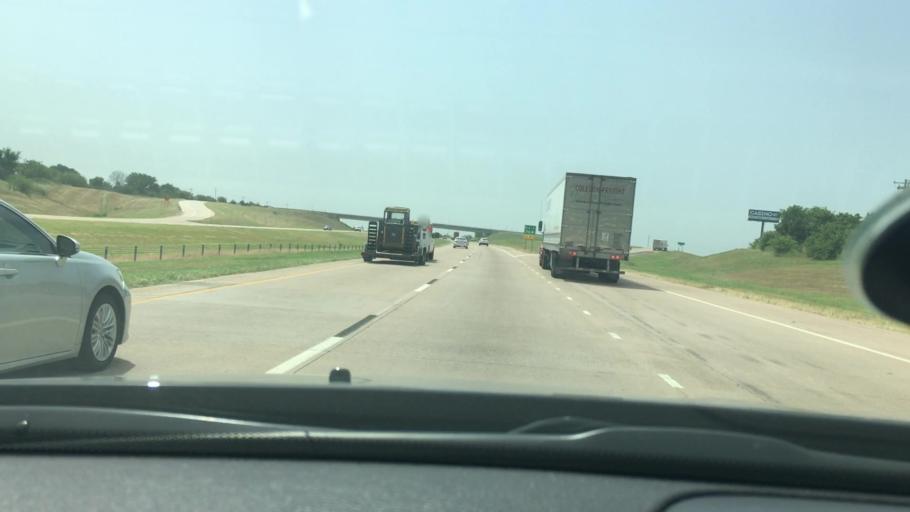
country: US
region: Oklahoma
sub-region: Garvin County
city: Pauls Valley
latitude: 34.7095
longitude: -97.2478
